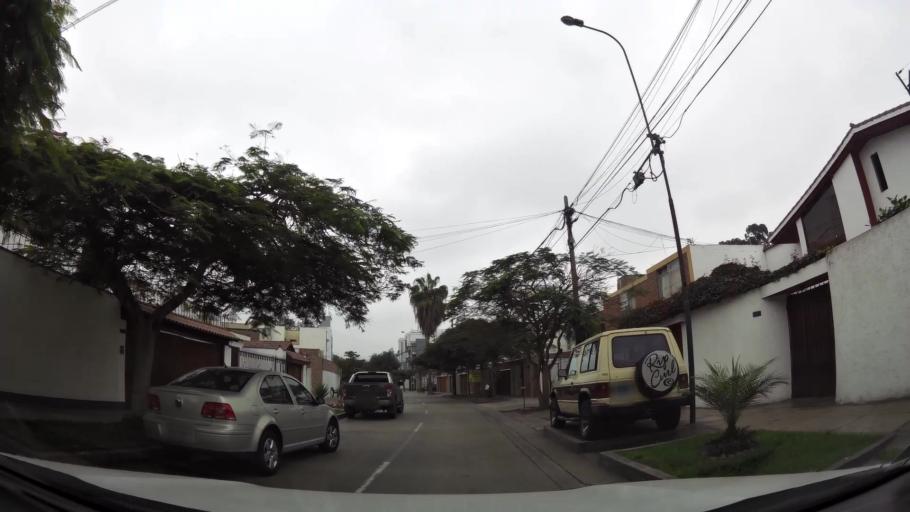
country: PE
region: Lima
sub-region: Lima
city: Surco
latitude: -12.1214
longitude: -76.9907
